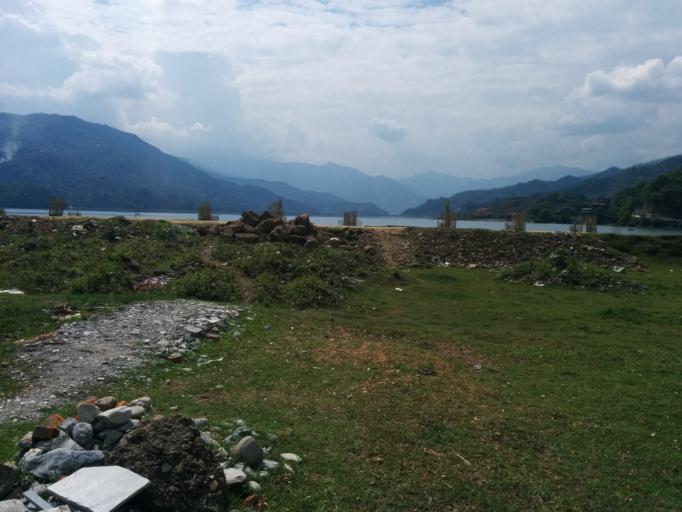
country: NP
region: Western Region
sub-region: Gandaki Zone
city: Pokhara
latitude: 28.2176
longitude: 83.9578
